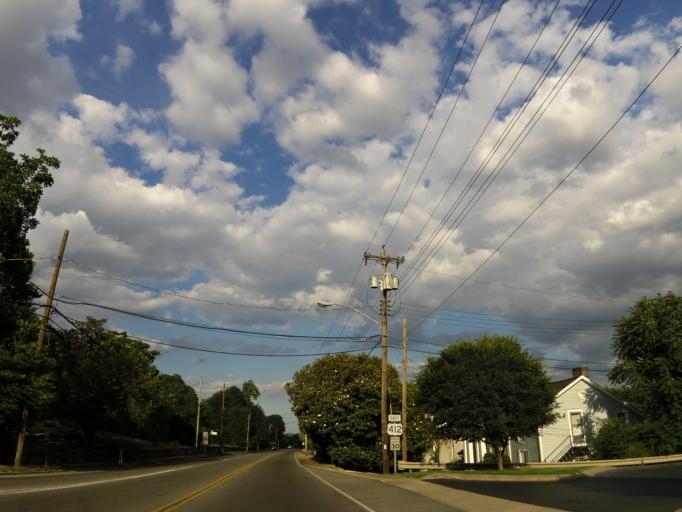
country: US
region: Tennessee
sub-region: Maury County
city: Columbia
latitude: 35.6159
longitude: -87.0454
